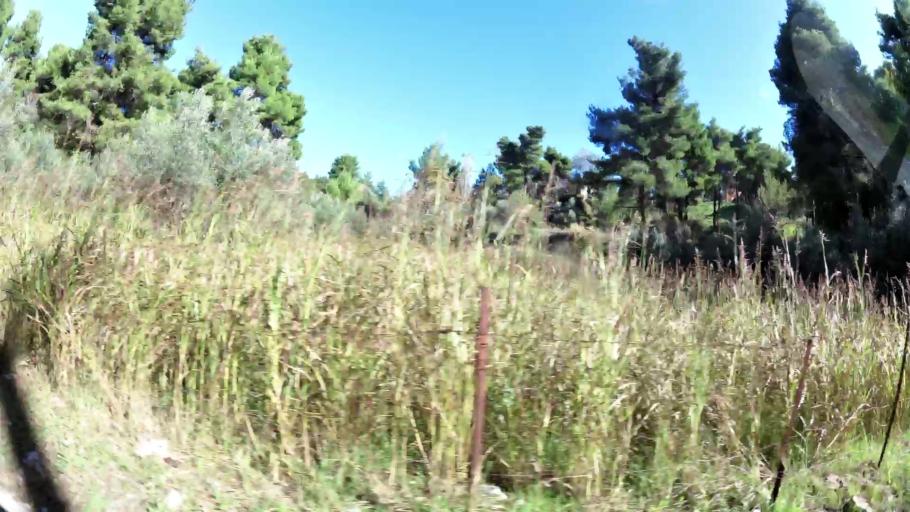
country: GR
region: Attica
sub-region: Nomarchia Anatolikis Attikis
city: Rodopoli
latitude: 38.1135
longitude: 23.8785
